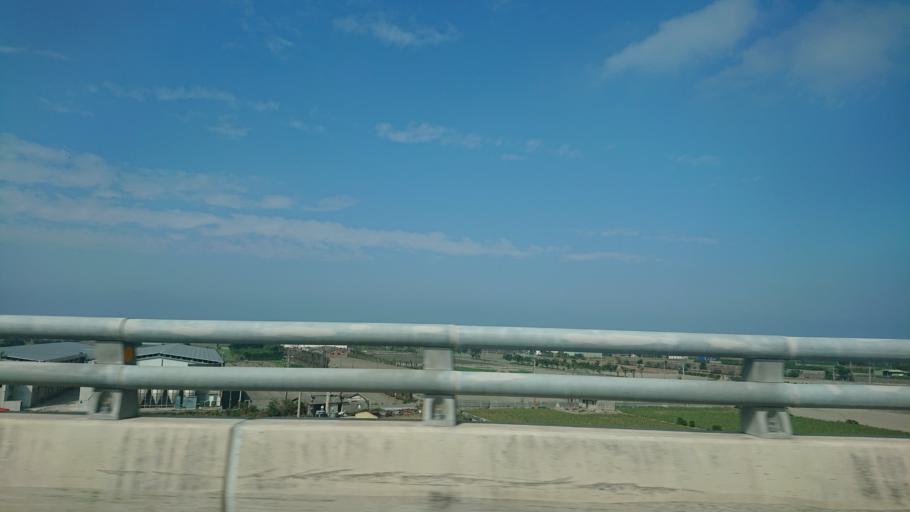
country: TW
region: Taiwan
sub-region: Changhua
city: Chang-hua
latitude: 23.9944
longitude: 120.3771
